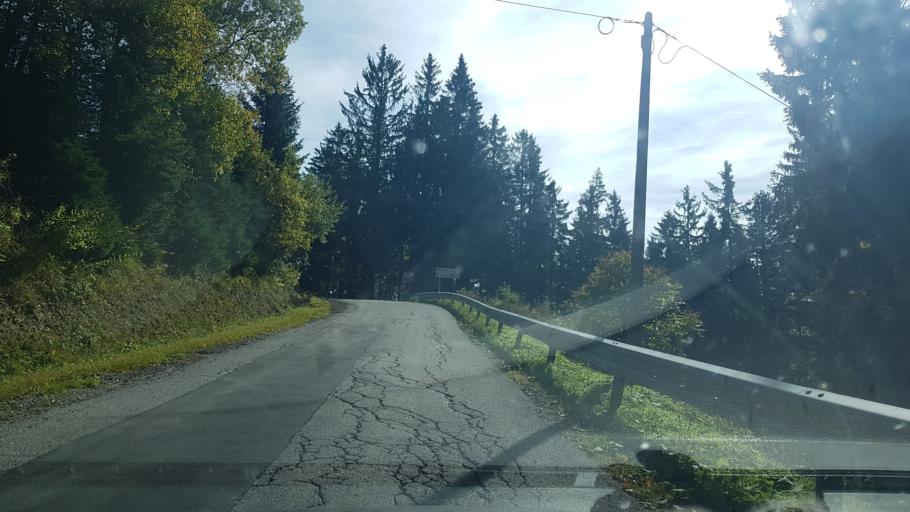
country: SI
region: Slovenj Gradec
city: Legen
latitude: 46.4981
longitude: 15.1980
